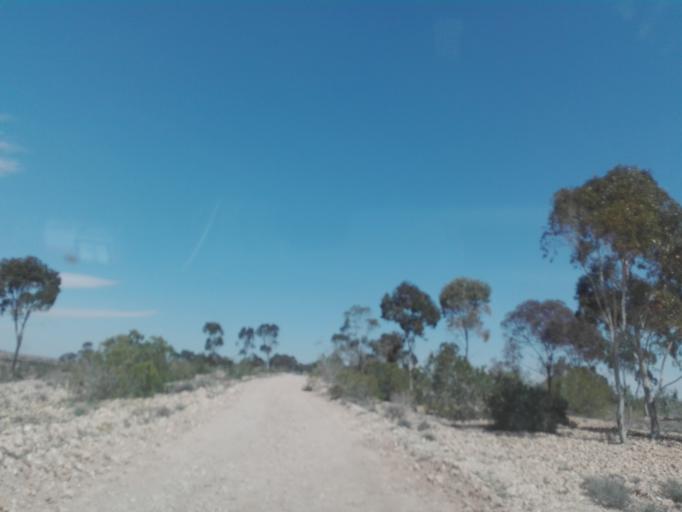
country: TN
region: Safaqis
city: Sfax
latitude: 34.7012
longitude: 10.5296
